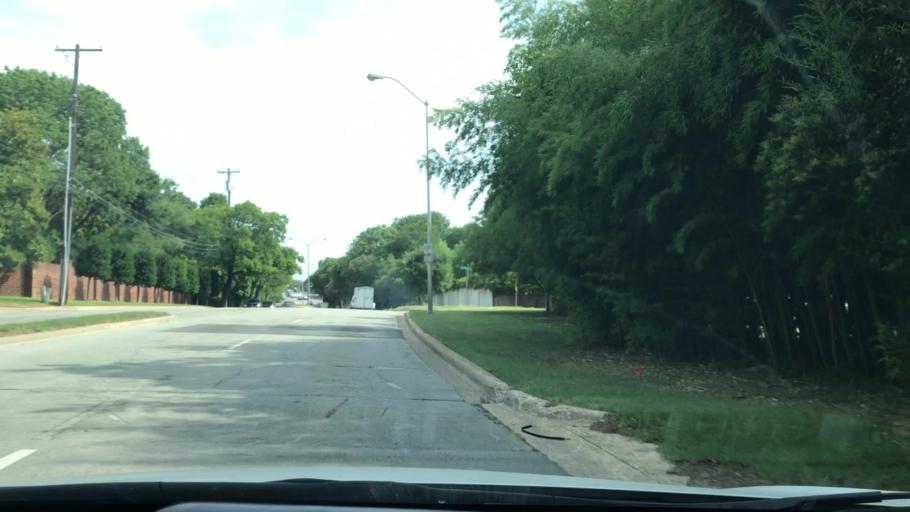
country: US
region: Texas
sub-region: Dallas County
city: University Park
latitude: 32.8772
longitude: -96.8212
